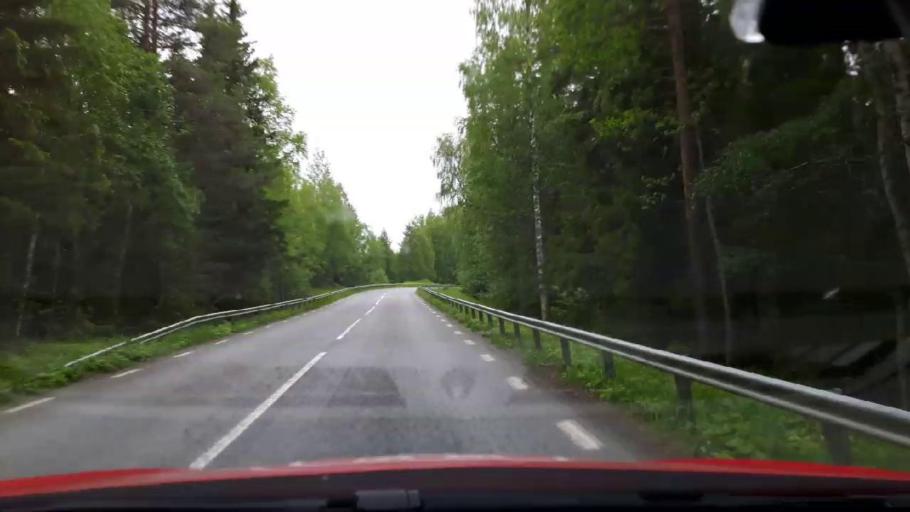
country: SE
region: Jaemtland
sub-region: Stroemsunds Kommun
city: Stroemsund
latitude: 63.5245
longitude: 15.4561
